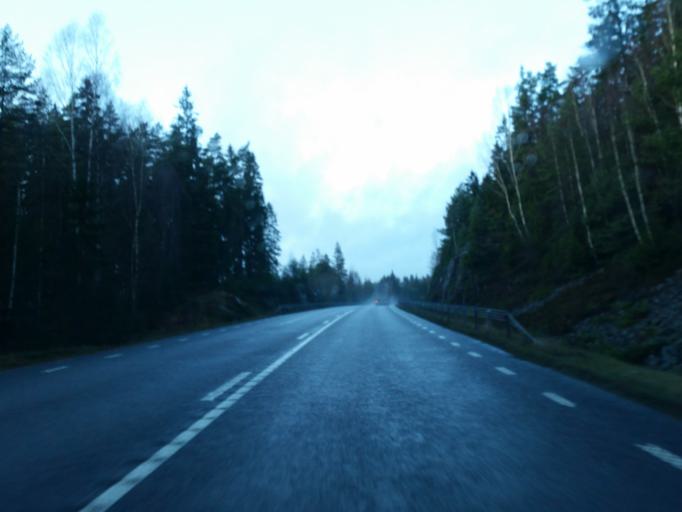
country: SE
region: Joenkoeping
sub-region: Gislaveds Kommun
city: Gislaved
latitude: 57.3303
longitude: 13.5267
